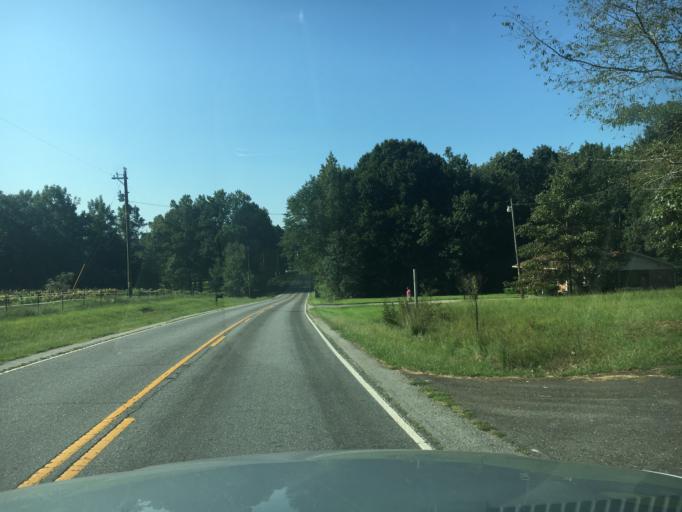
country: US
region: South Carolina
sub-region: Anderson County
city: Williamston
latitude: 34.6066
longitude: -82.3480
